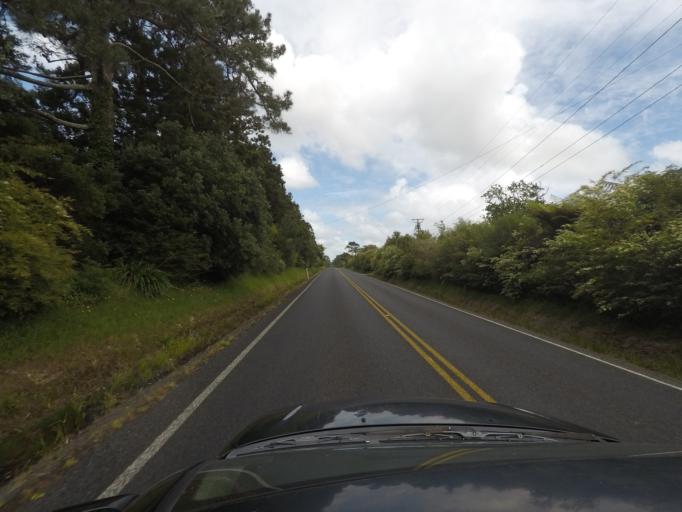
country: NZ
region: Auckland
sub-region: Auckland
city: Parakai
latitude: -36.6443
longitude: 174.5141
